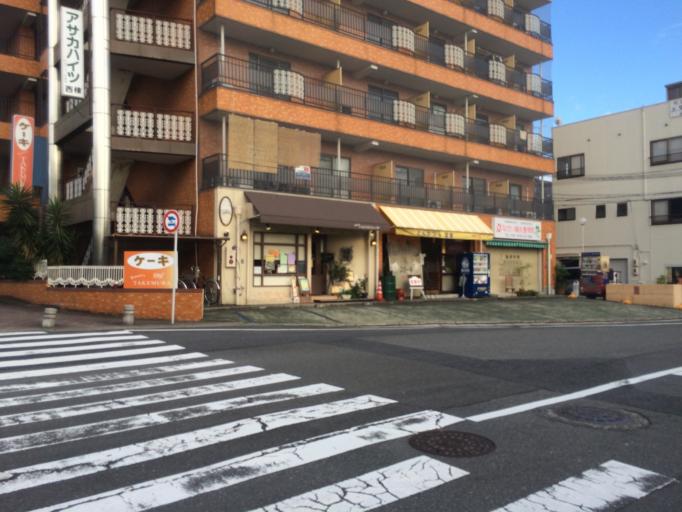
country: JP
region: Nara
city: Nara-shi
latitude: 34.6739
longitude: 135.8386
